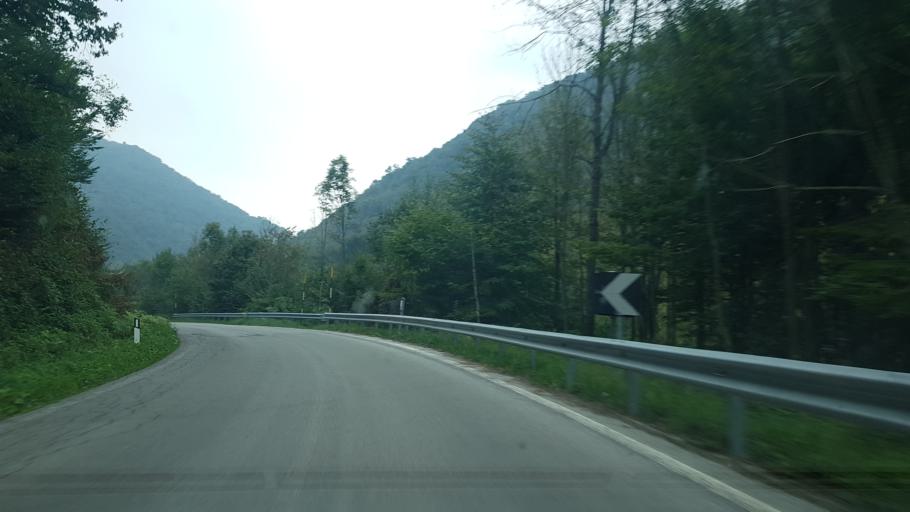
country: IT
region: Piedmont
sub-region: Provincia di Cuneo
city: Roccaforte Mondovi
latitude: 44.2805
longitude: 7.7461
